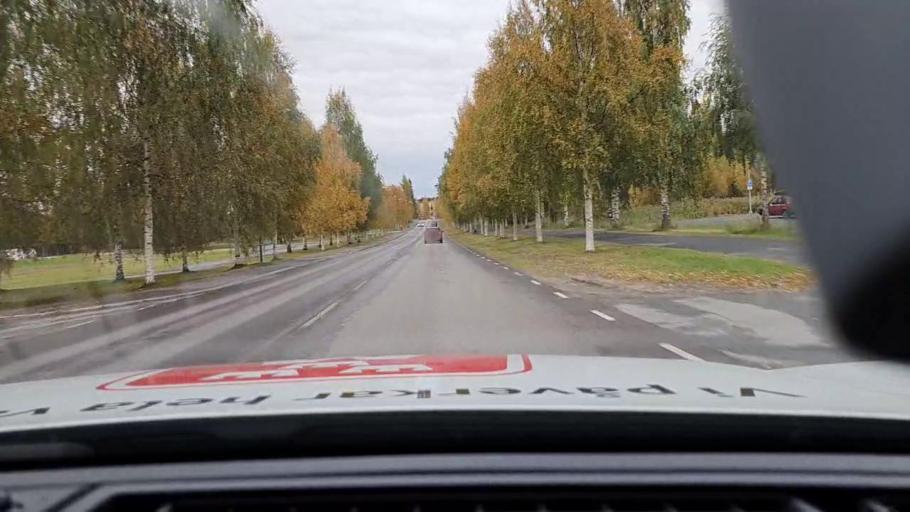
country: SE
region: Norrbotten
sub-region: Bodens Kommun
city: Boden
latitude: 65.8170
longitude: 21.6690
